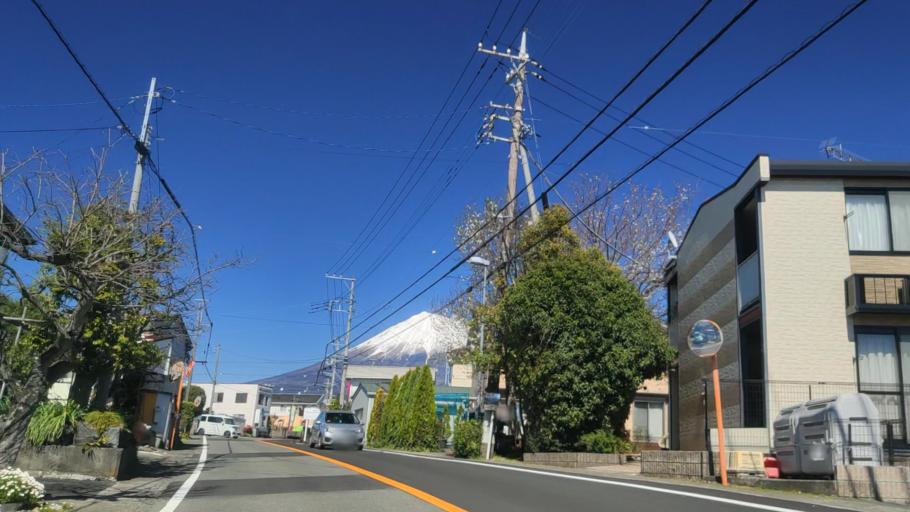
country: JP
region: Shizuoka
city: Fujinomiya
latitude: 35.2143
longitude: 138.6373
